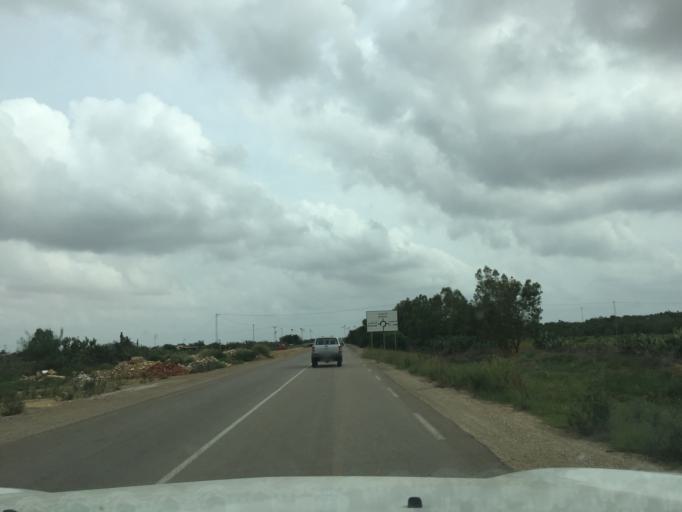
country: TN
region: Al Munastir
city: Sidi Bin Nur
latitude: 35.5428
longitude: 10.8612
